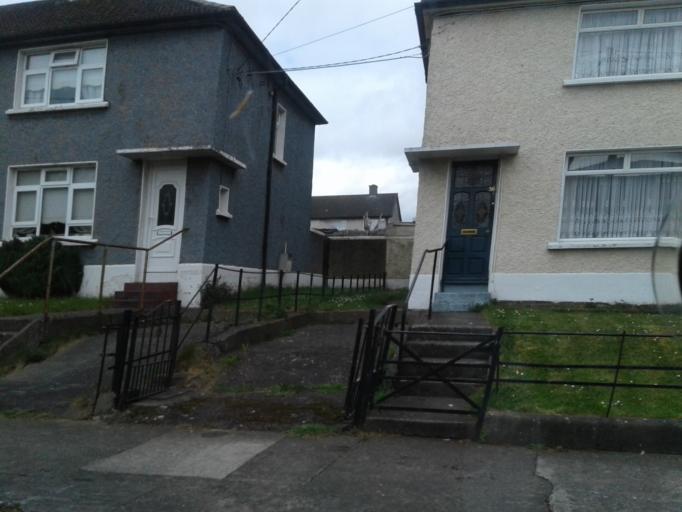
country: IE
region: Leinster
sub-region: Dublin City
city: Finglas
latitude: 53.3912
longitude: -6.3134
